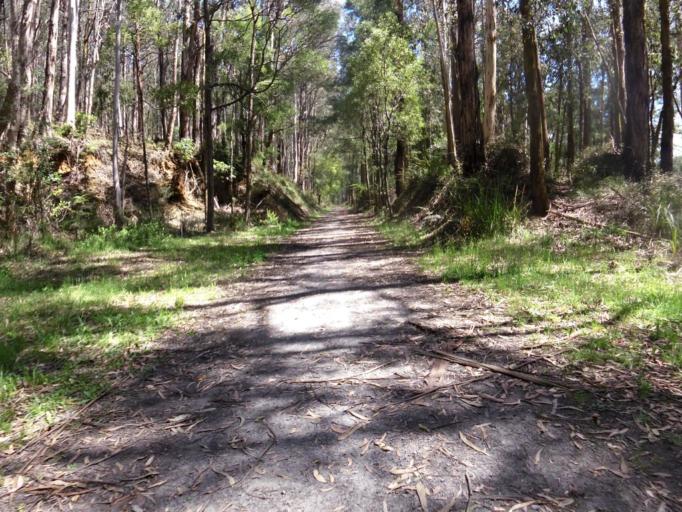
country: AU
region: Victoria
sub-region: Baw Baw
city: Warragul
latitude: -37.8964
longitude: 145.9910
